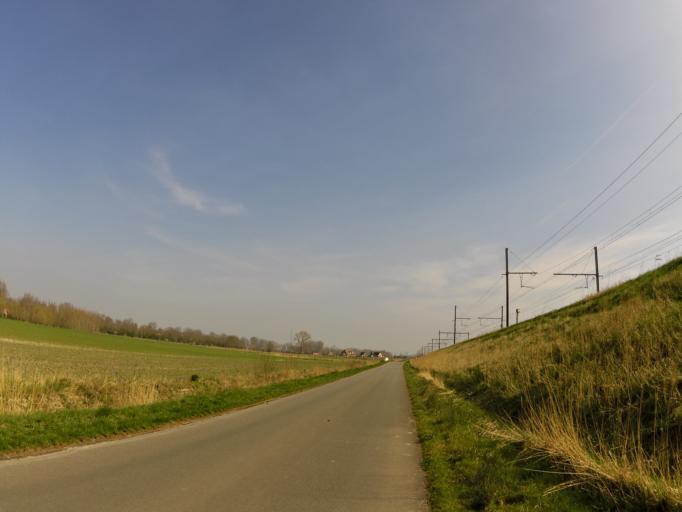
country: BE
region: Flanders
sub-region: Provincie West-Vlaanderen
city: Oudenburg
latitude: 51.2047
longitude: 3.0131
